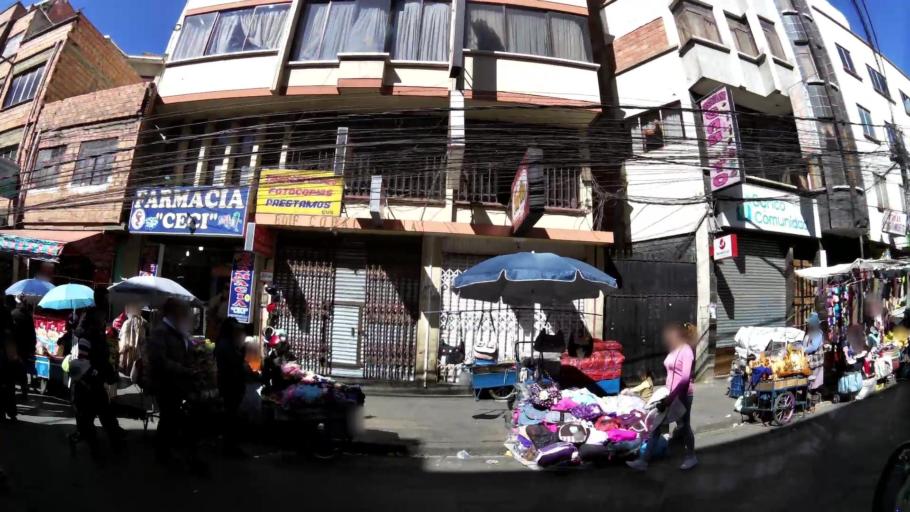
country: BO
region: La Paz
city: La Paz
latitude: -16.4963
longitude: -68.1444
